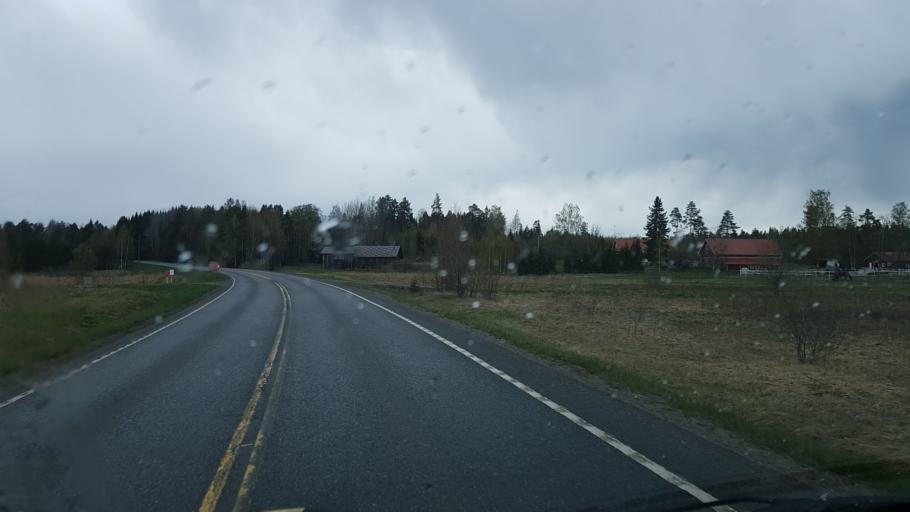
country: FI
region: Pirkanmaa
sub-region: Tampere
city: Pirkkala
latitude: 61.4252
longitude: 23.6342
